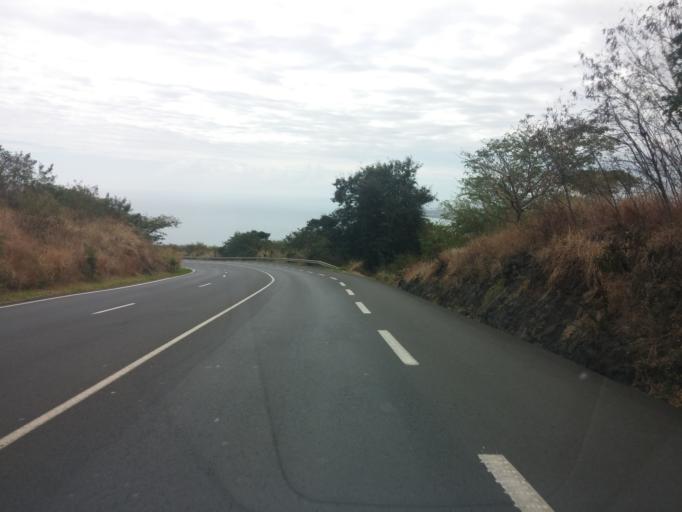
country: RE
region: Reunion
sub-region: Reunion
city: Saint-Paul
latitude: -21.0227
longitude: 55.2737
